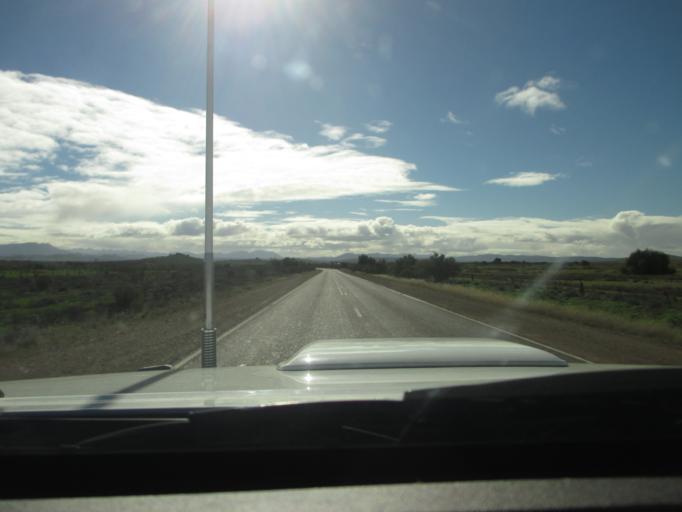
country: AU
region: South Australia
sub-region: Flinders Ranges
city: Quorn
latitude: -31.9118
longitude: 138.4315
